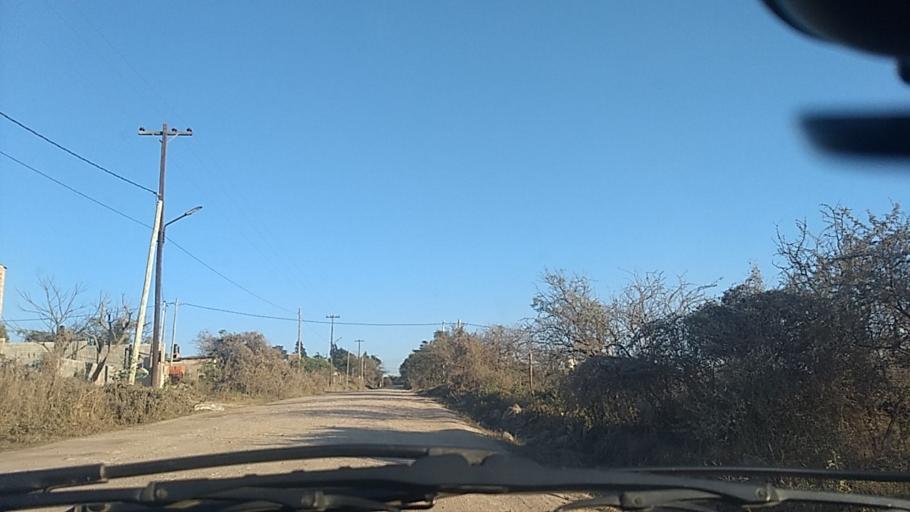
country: AR
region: Cordoba
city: Salsipuedes
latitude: -31.1408
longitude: -64.2858
